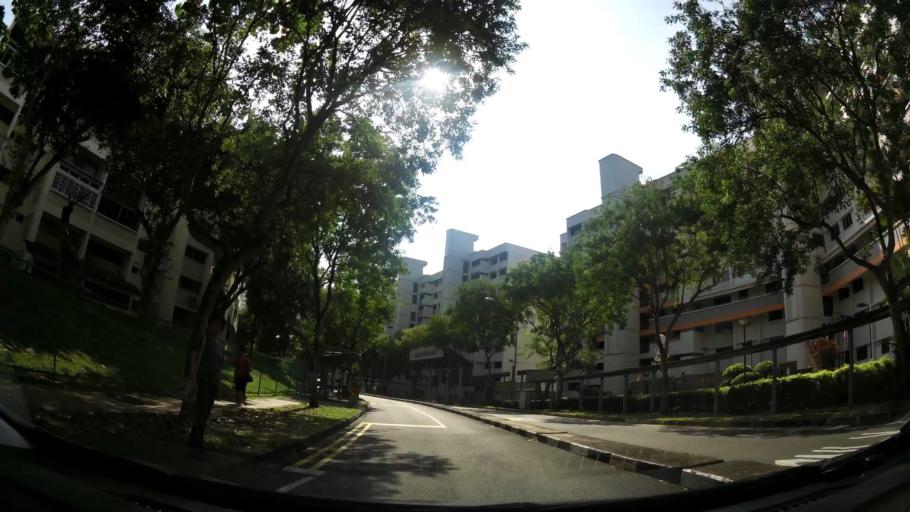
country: SG
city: Singapore
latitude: 1.3517
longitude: 103.8377
